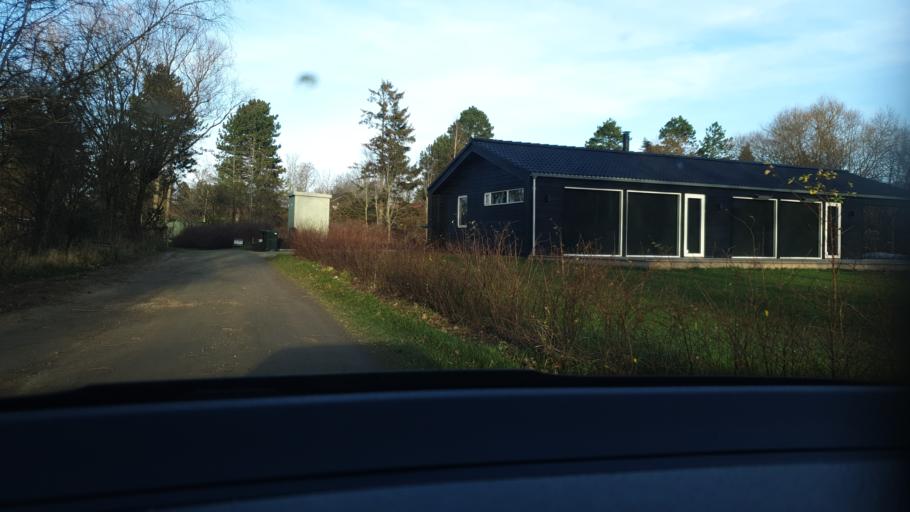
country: DK
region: Zealand
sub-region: Odsherred Kommune
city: Hojby
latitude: 55.9322
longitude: 11.6231
